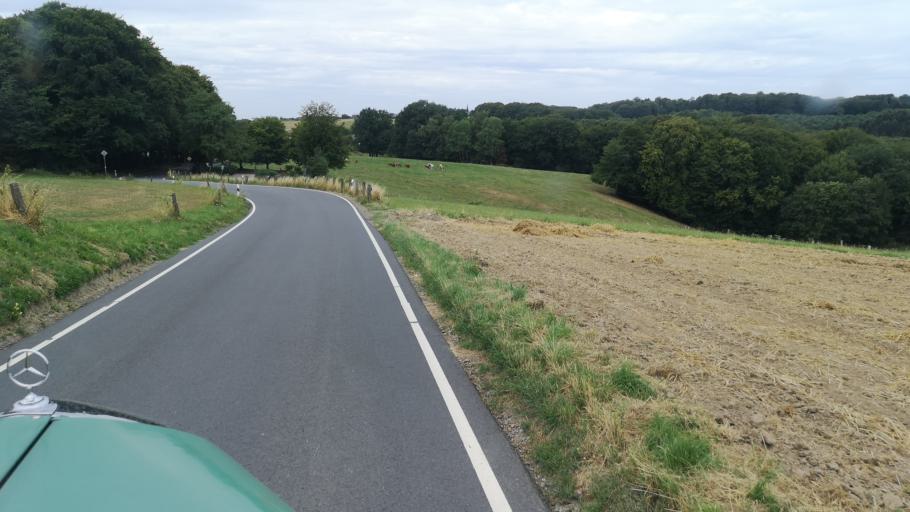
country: DE
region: North Rhine-Westphalia
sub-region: Regierungsbezirk Koln
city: Kurten
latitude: 51.0489
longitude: 7.1956
